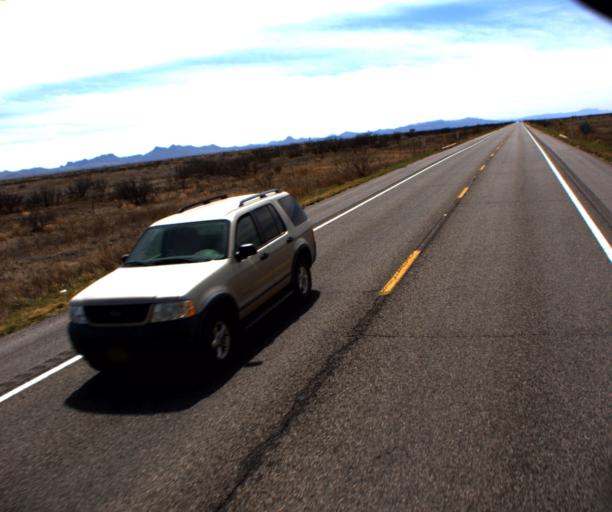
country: US
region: Arizona
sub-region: Cochise County
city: Pirtleville
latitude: 31.4991
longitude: -109.6344
